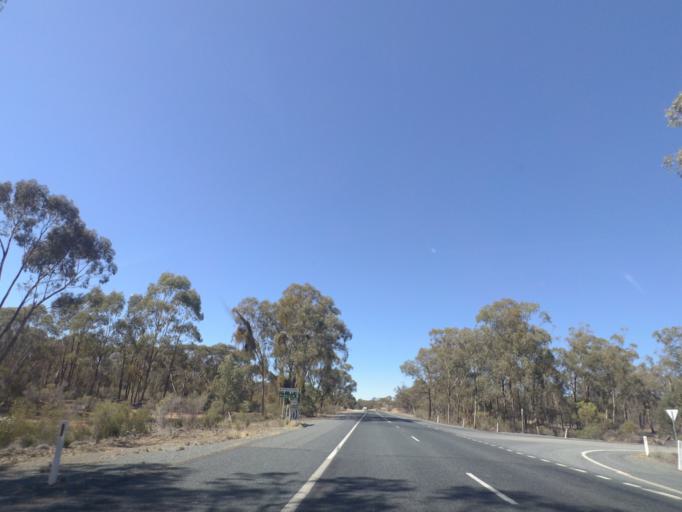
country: AU
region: New South Wales
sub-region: Bland
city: West Wyalong
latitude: -34.1363
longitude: 147.1216
